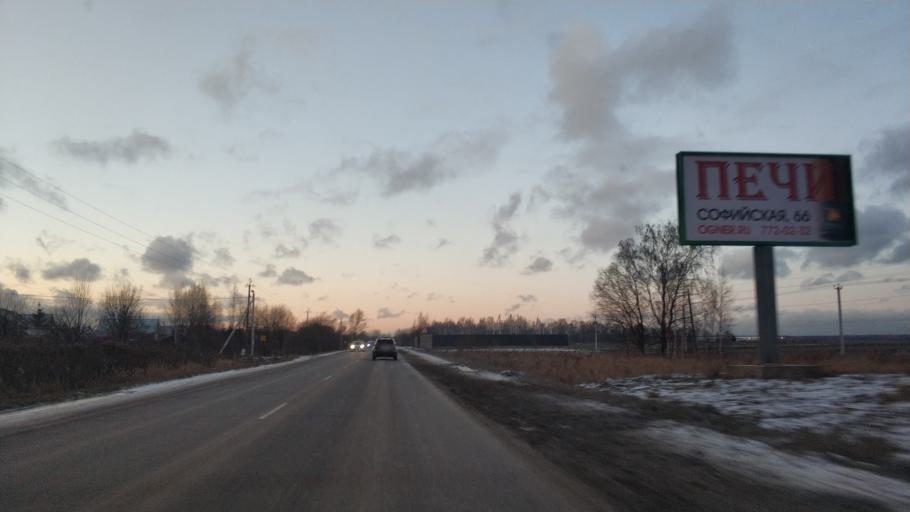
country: RU
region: St.-Petersburg
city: Pontonnyy
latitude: 59.8028
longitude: 30.6307
